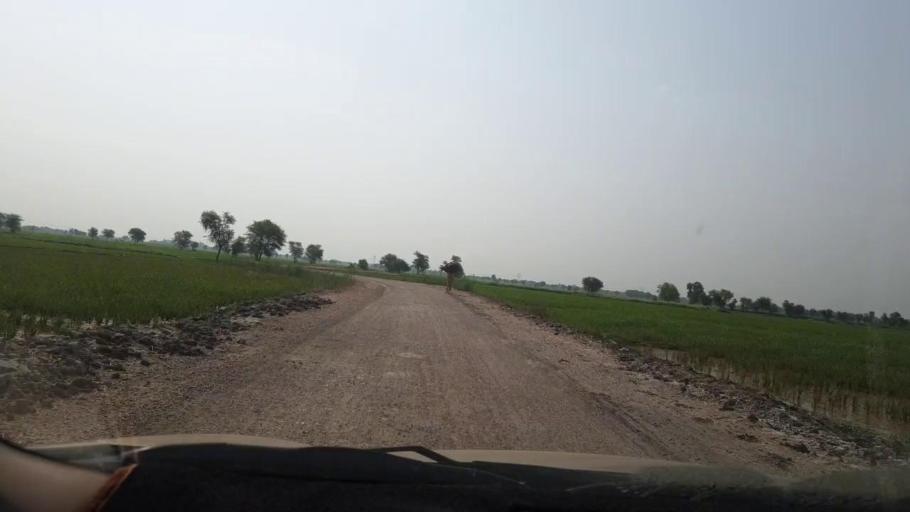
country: PK
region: Sindh
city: Goth Garelo
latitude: 27.4455
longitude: 68.0364
